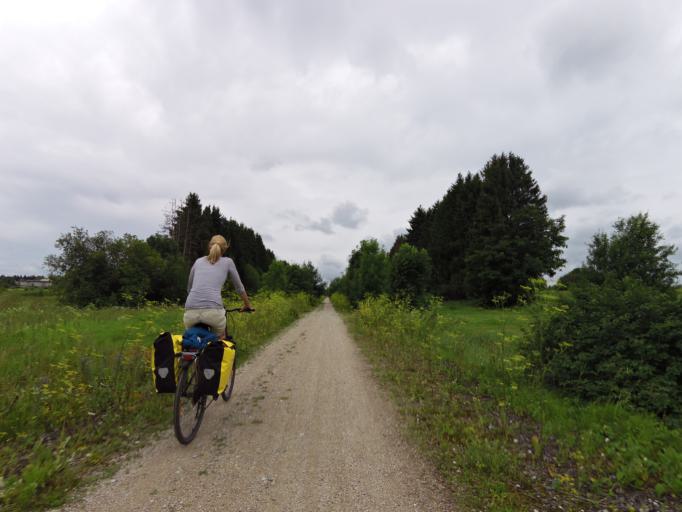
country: EE
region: Harju
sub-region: Nissi vald
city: Turba
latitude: 59.0024
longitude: 24.0640
